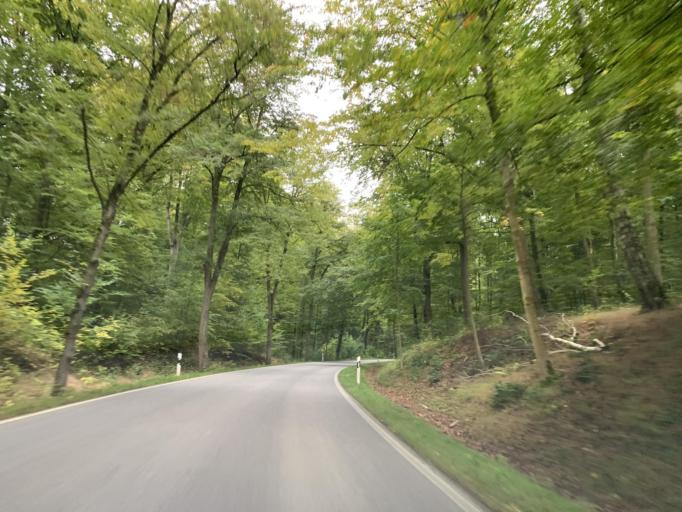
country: DE
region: Mecklenburg-Vorpommern
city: Burg Stargard
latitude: 53.4884
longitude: 13.3001
